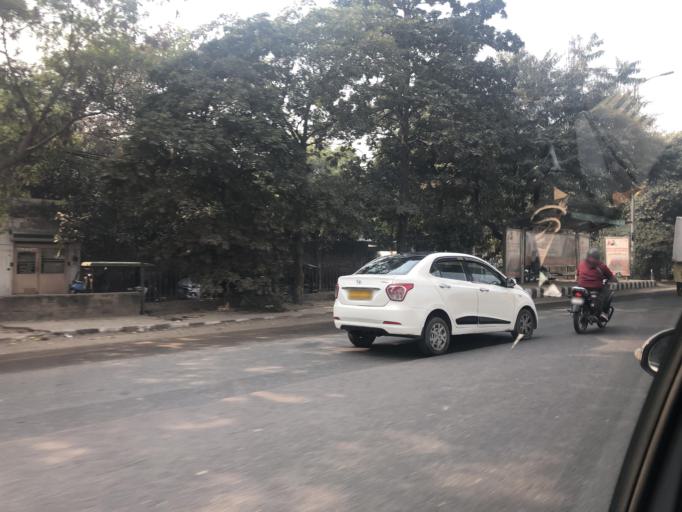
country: IN
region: NCT
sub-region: North West Delhi
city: Pitampura
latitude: 28.6756
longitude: 77.1256
